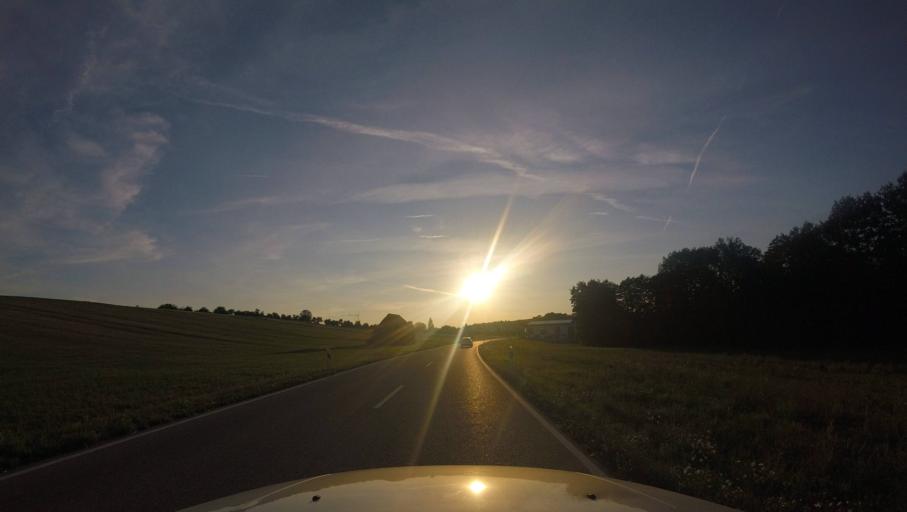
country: DE
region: Baden-Wuerttemberg
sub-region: Regierungsbezirk Stuttgart
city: Rudersberg
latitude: 48.9199
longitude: 9.5103
